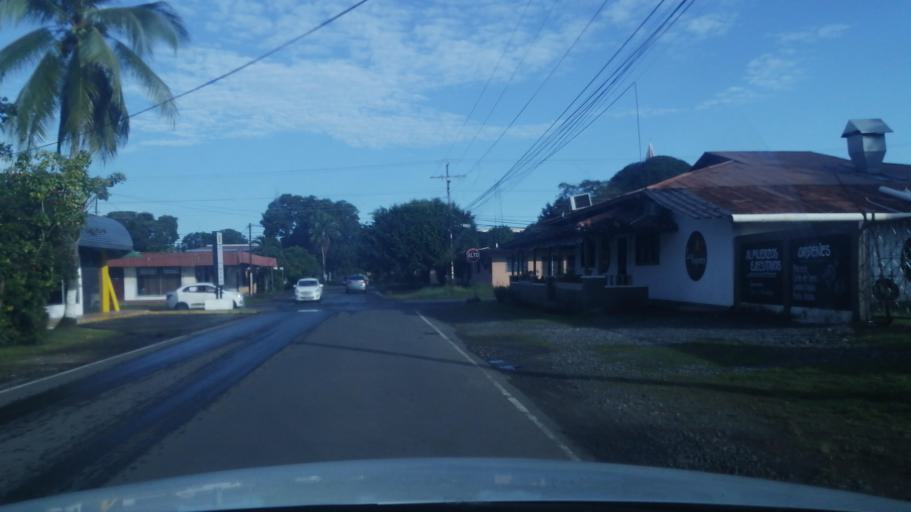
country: PA
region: Chiriqui
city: David
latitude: 8.4215
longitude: -82.4310
